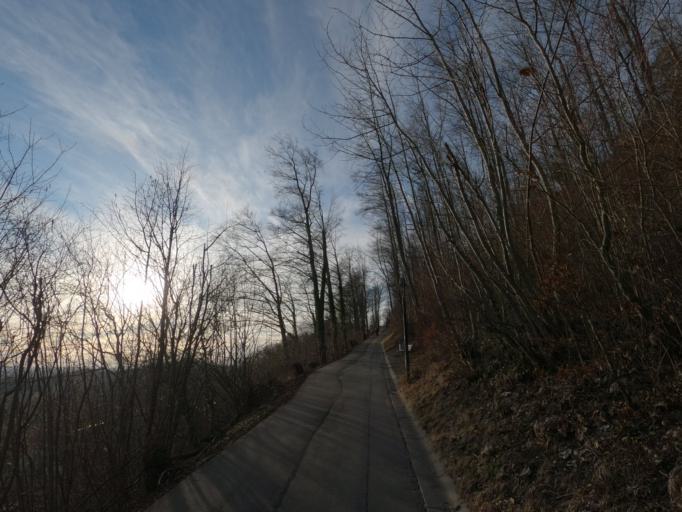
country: DE
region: Baden-Wuerttemberg
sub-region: Regierungsbezirk Stuttgart
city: Waldstetten
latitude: 48.7553
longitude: 9.7861
